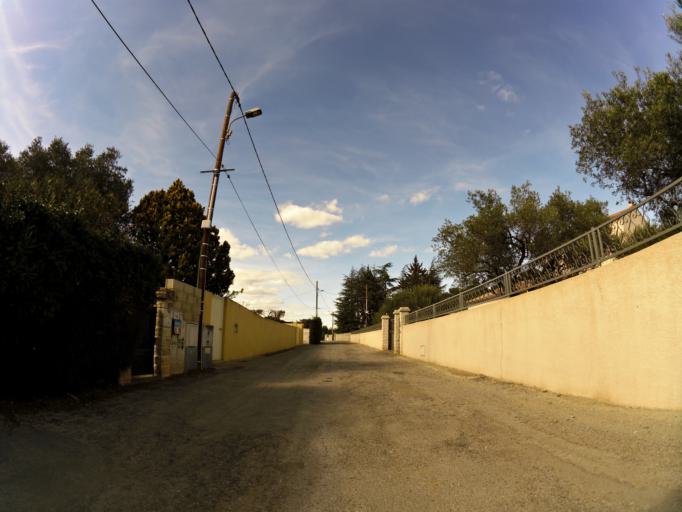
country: FR
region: Languedoc-Roussillon
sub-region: Departement du Gard
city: Mus
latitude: 43.7437
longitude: 4.2009
